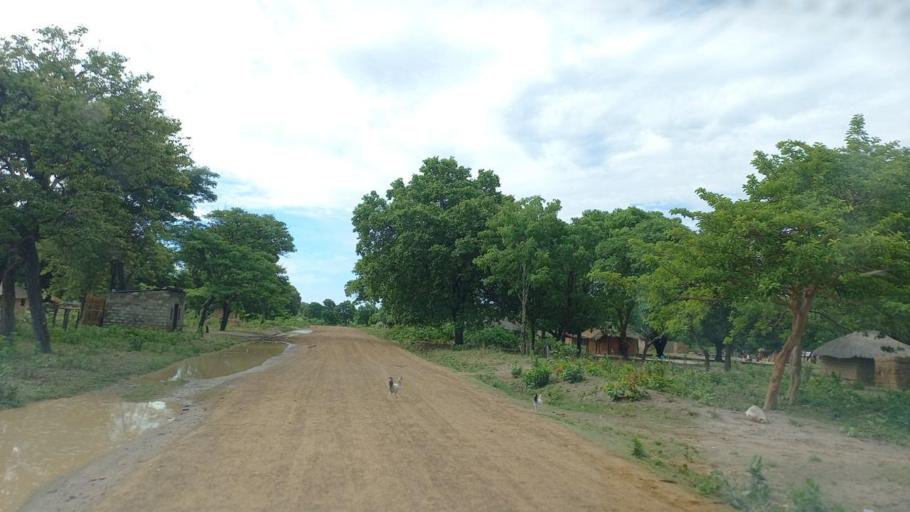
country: ZM
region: North-Western
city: Kabompo
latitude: -13.4615
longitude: 24.4272
